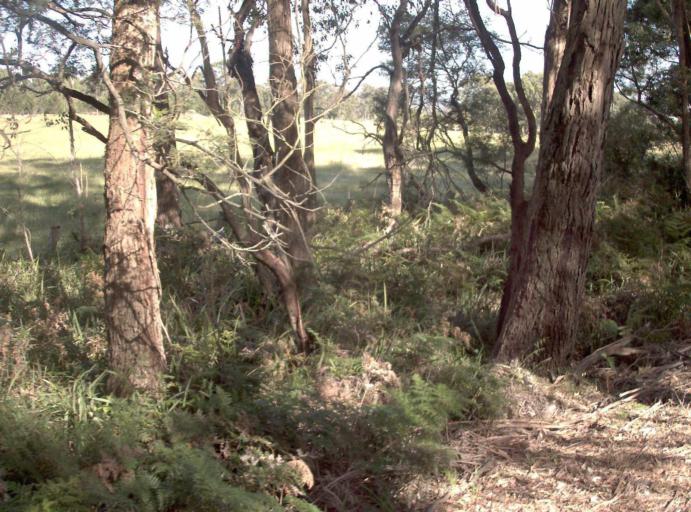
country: AU
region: Victoria
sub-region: East Gippsland
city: Lakes Entrance
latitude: -37.7479
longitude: 147.8140
